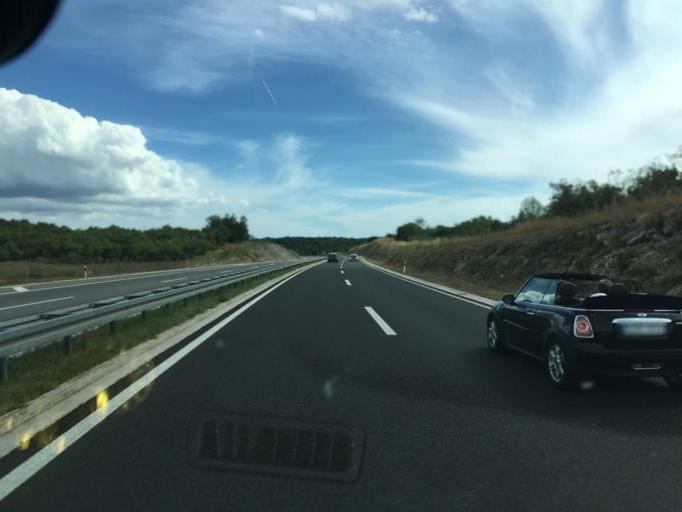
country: HR
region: Istarska
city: Vodnjan
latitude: 45.0695
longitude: 13.8416
